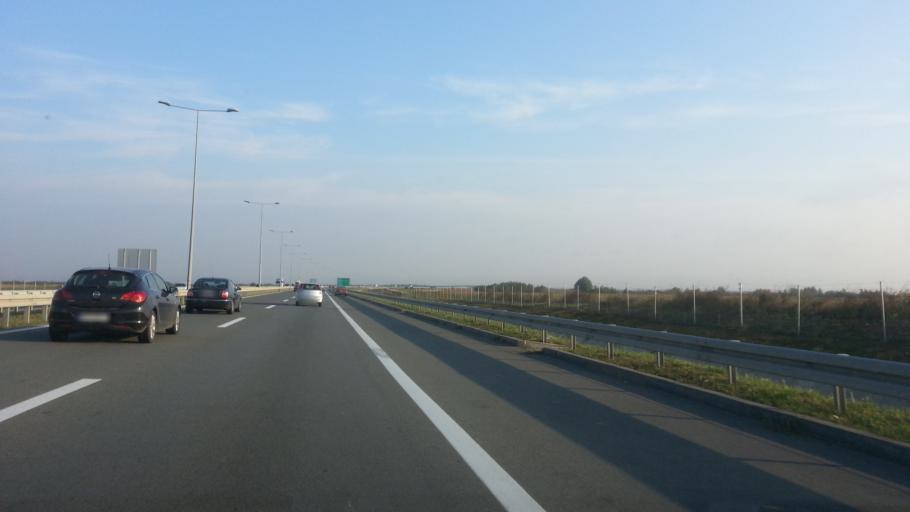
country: RS
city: Dobanovci
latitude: 44.8463
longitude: 20.2496
